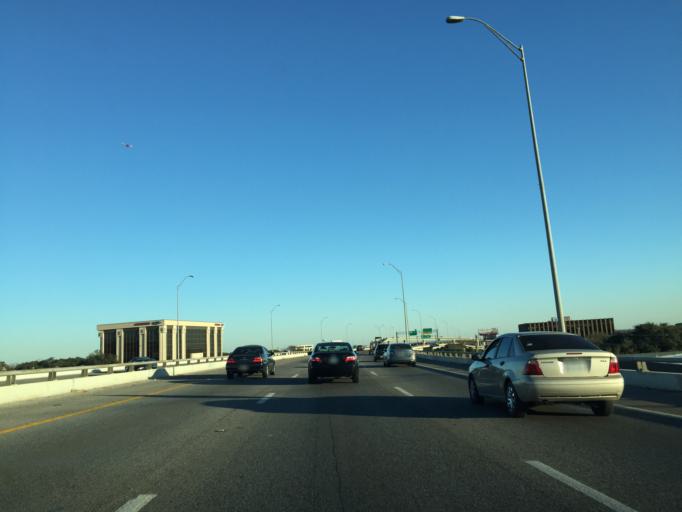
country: US
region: Texas
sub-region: Travis County
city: Austin
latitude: 30.3438
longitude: -97.7052
